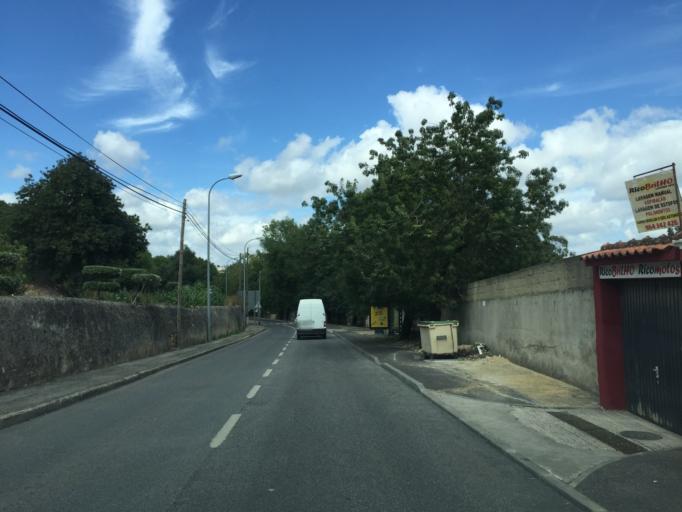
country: PT
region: Lisbon
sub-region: Odivelas
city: Famoes
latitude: 38.7883
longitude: -9.2338
